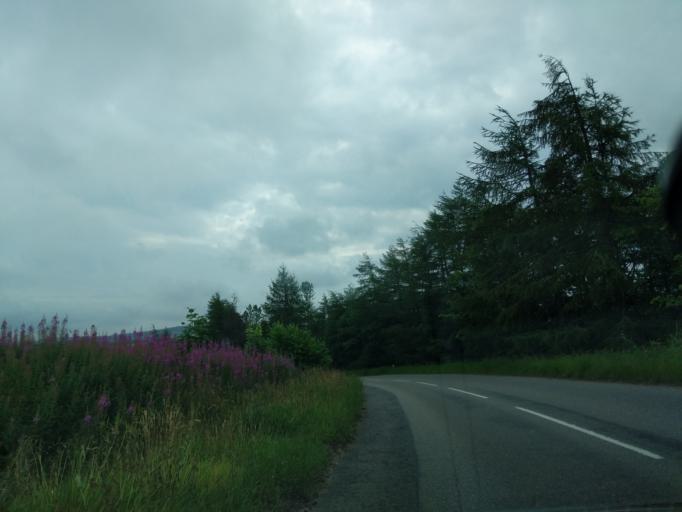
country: GB
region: Scotland
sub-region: Moray
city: Rothes
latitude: 57.4903
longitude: -3.2077
